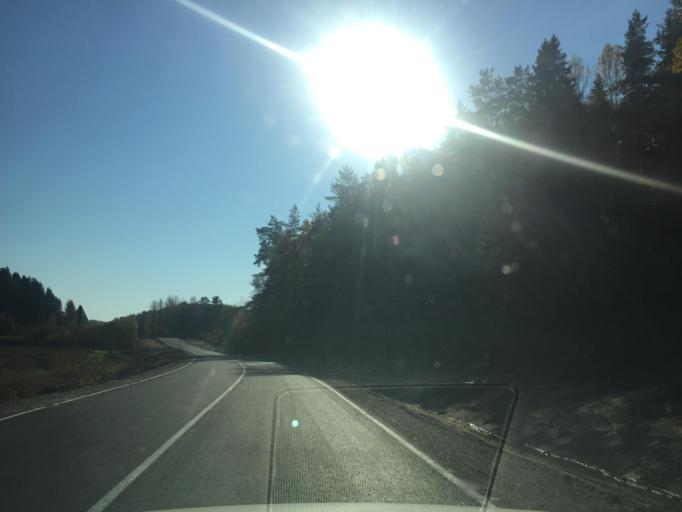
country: RU
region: Leningrad
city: Kuznechnoye
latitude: 61.3199
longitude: 29.8683
